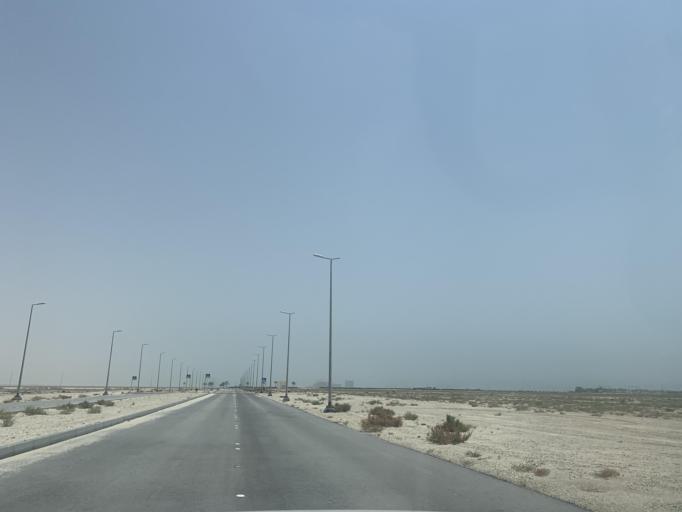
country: BH
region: Central Governorate
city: Dar Kulayb
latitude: 25.8427
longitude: 50.5890
